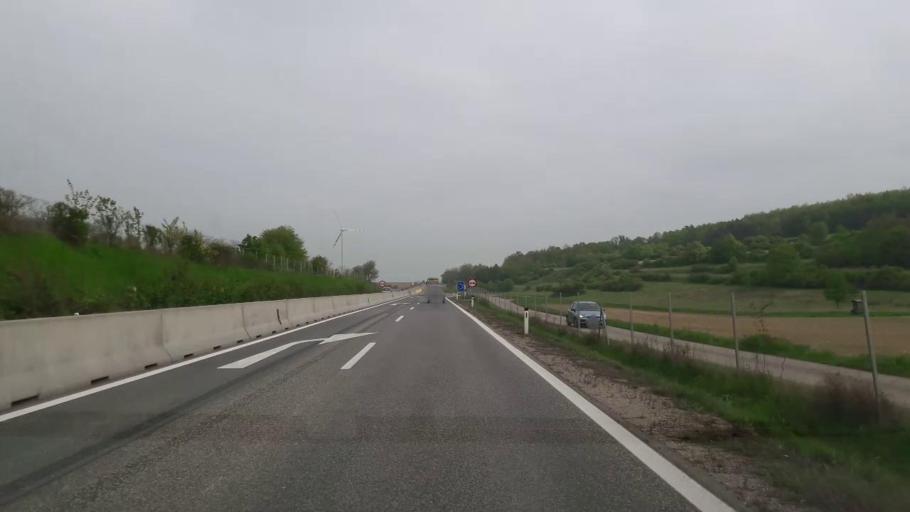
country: AT
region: Lower Austria
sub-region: Politischer Bezirk Hollabrunn
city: Hollabrunn
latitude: 48.5197
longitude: 16.0855
